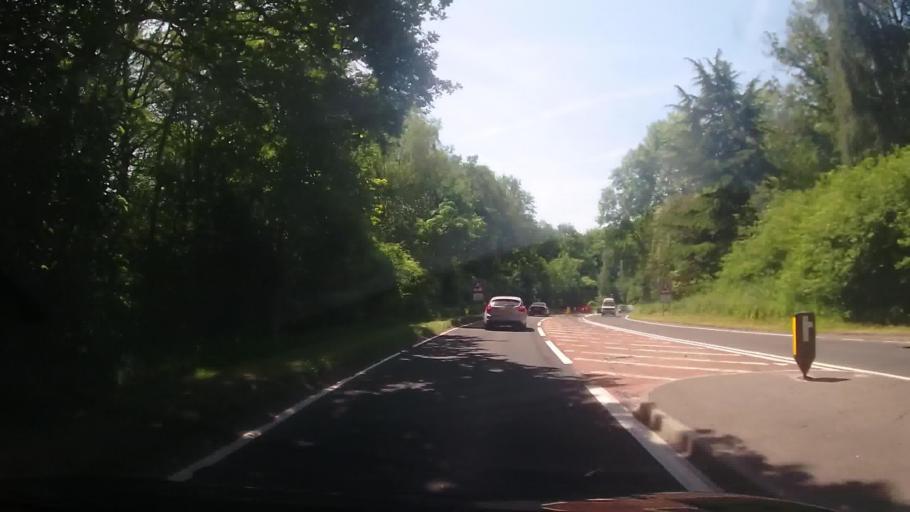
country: GB
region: England
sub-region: Herefordshire
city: Hope under Dinmore
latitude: 52.1594
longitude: -2.7213
